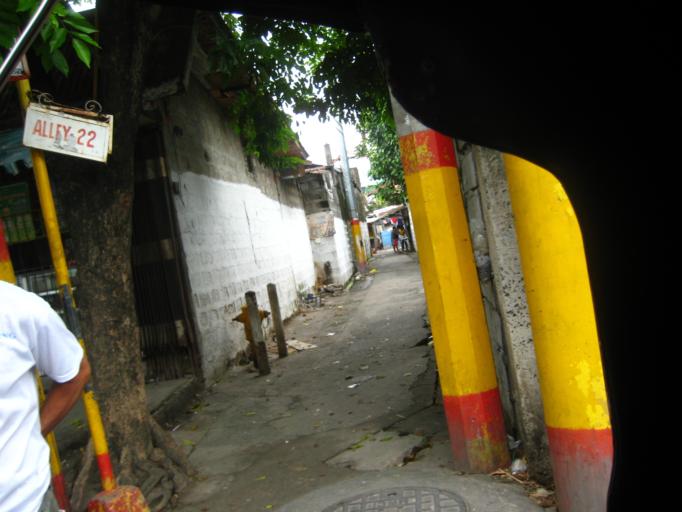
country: PH
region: Calabarzon
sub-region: Province of Rizal
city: Pateros
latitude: 14.5470
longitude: 121.0761
